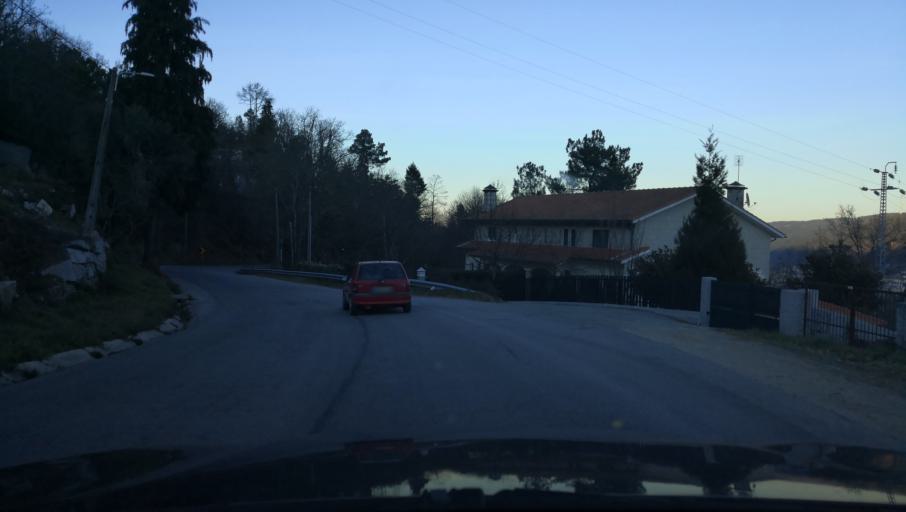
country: PT
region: Vila Real
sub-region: Vila Pouca de Aguiar
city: Vila Pouca de Aguiar
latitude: 41.4958
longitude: -7.6516
